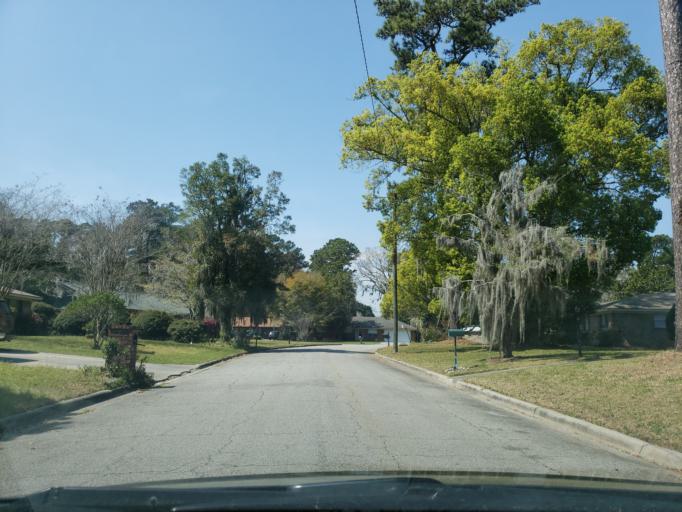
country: US
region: Georgia
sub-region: Chatham County
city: Montgomery
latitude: 31.9951
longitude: -81.1393
